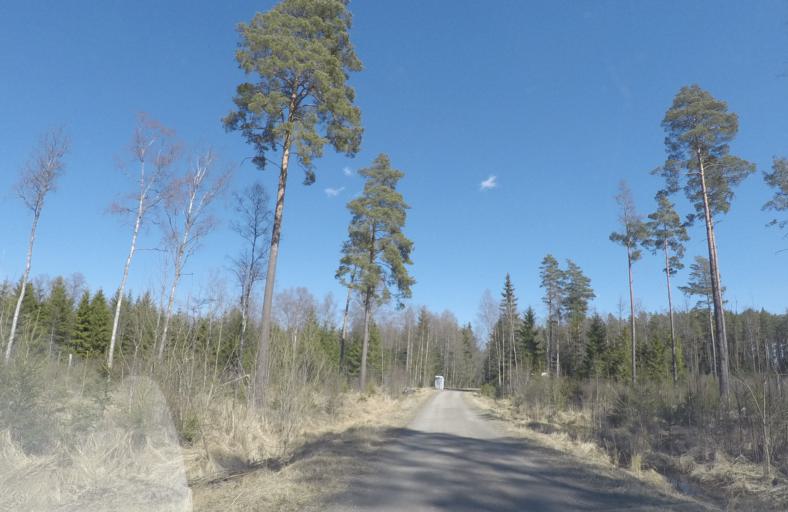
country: SE
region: Vaestmanland
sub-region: Vasteras
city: Vasteras
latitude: 59.6738
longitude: 16.5106
